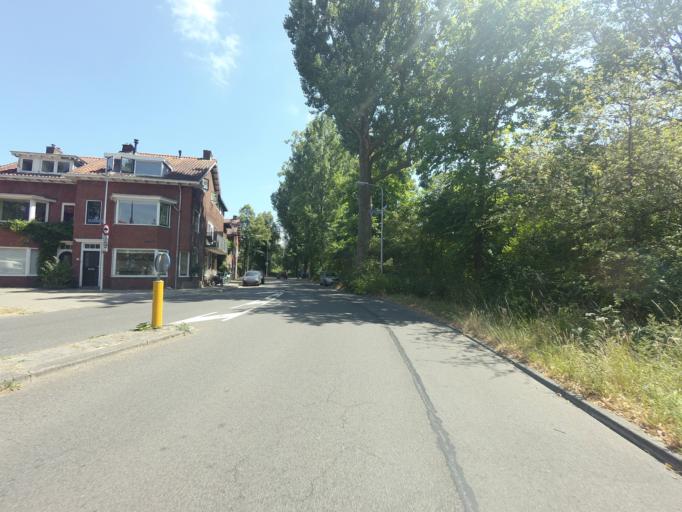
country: NL
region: Utrecht
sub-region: Gemeente Utrecht
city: Lunetten
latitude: 52.0607
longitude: 5.1160
